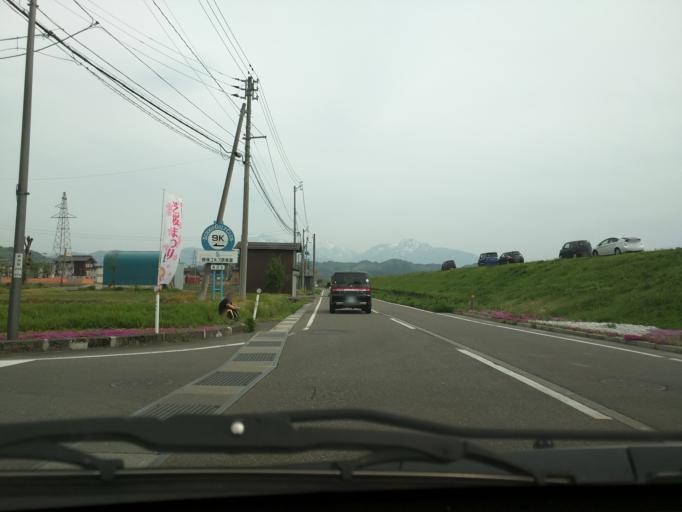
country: JP
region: Niigata
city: Ojiya
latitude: 37.2540
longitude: 138.9211
